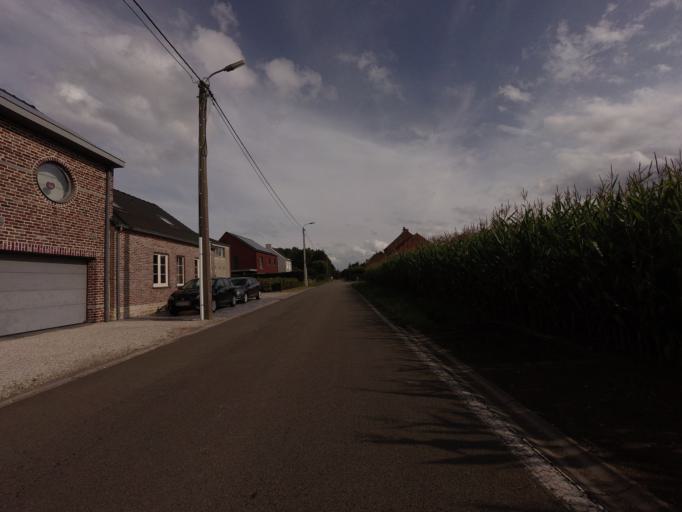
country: BE
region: Flanders
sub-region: Provincie Vlaams-Brabant
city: Kapelle-op-den-Bos
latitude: 51.0255
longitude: 4.3734
